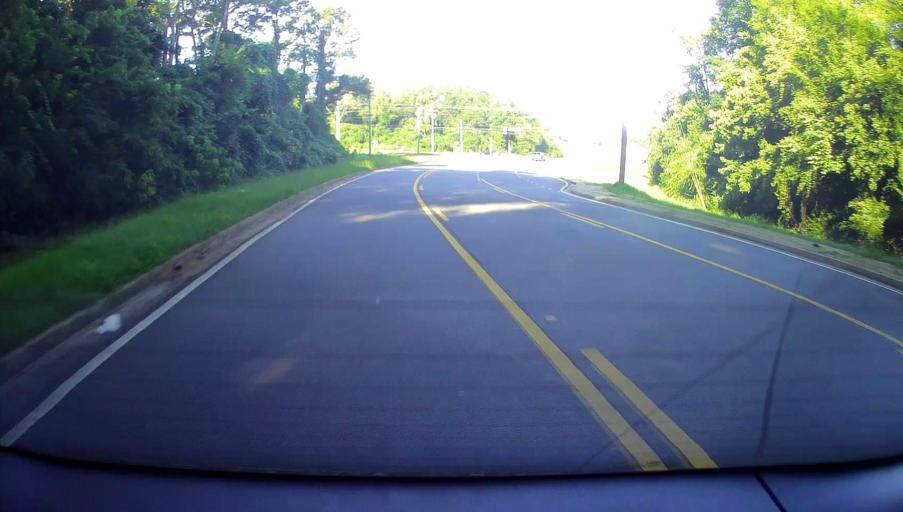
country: US
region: Georgia
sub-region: Houston County
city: Centerville
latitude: 32.6330
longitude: -83.7076
